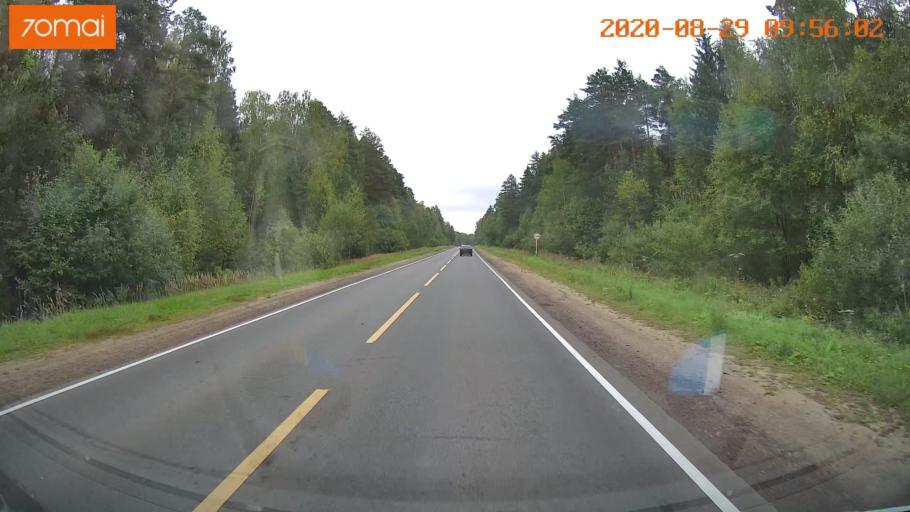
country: RU
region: Ivanovo
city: Zarechnyy
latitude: 57.4214
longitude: 42.2787
